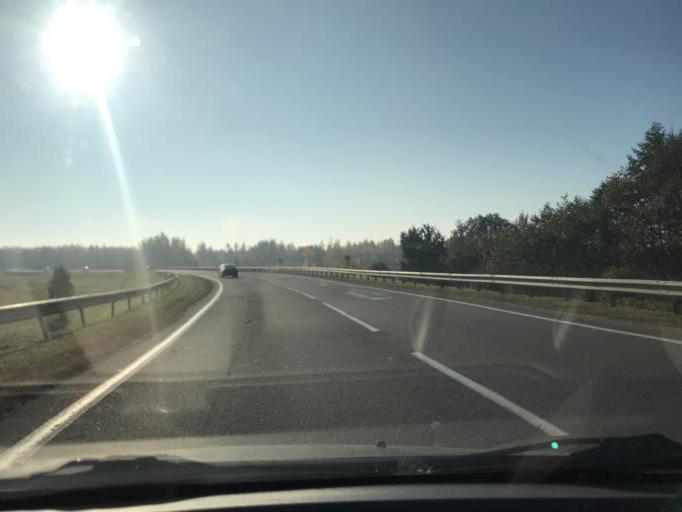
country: BY
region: Minsk
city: Dukora
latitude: 53.6634
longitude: 27.9399
